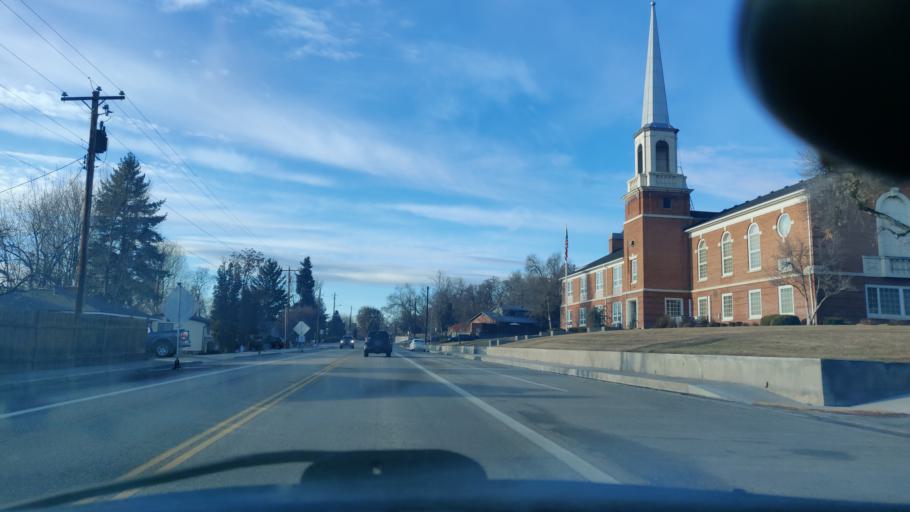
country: US
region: Idaho
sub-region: Ada County
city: Garden City
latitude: 43.6481
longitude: -116.2216
